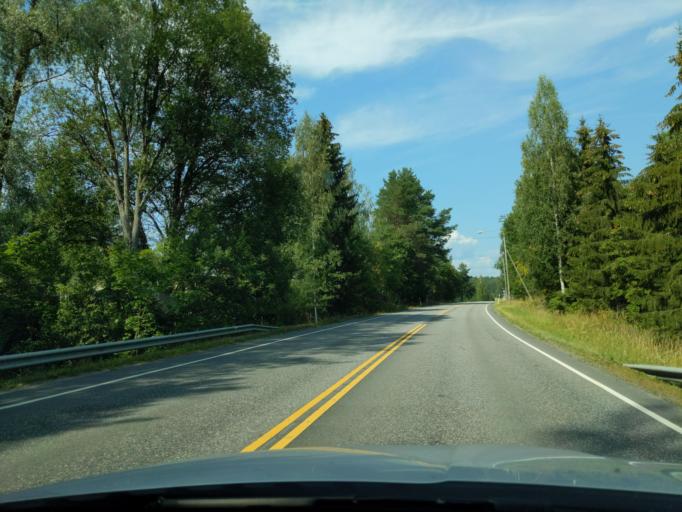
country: FI
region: Paijanne Tavastia
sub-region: Lahti
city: Padasjoki
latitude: 61.3833
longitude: 25.1905
